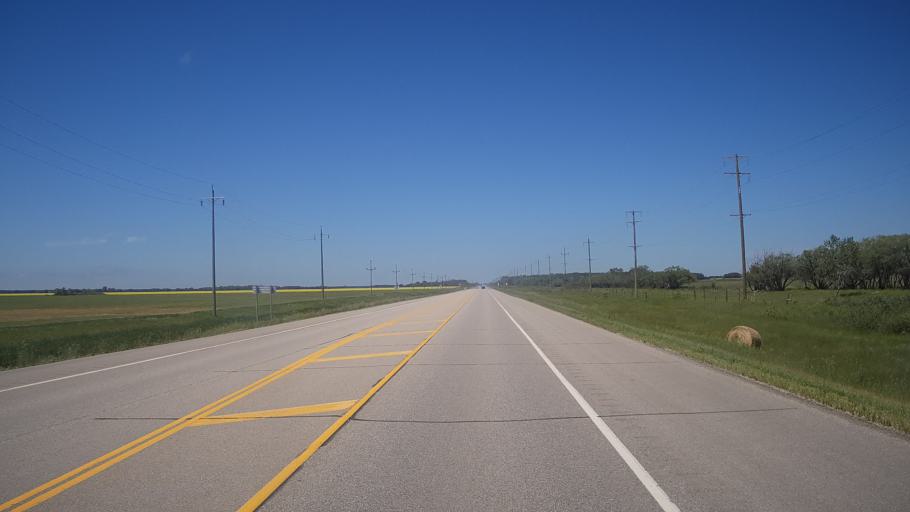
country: CA
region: Manitoba
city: Neepawa
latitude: 50.2258
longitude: -99.0785
